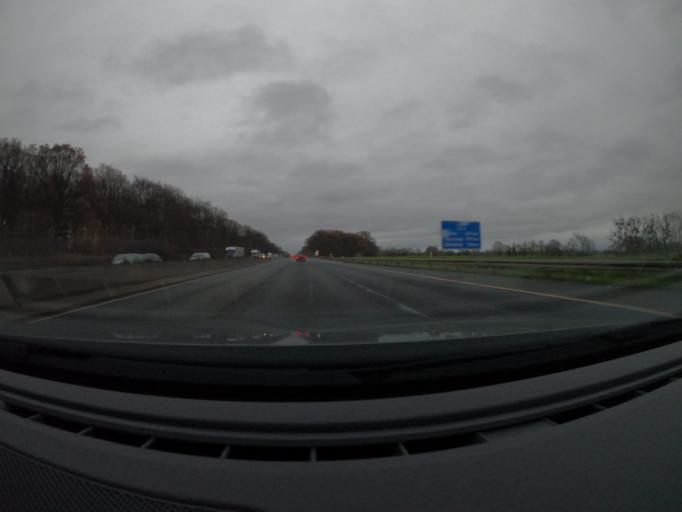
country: DE
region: North Rhine-Westphalia
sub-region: Regierungsbezirk Arnsberg
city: Bonen
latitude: 51.6019
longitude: 7.7155
